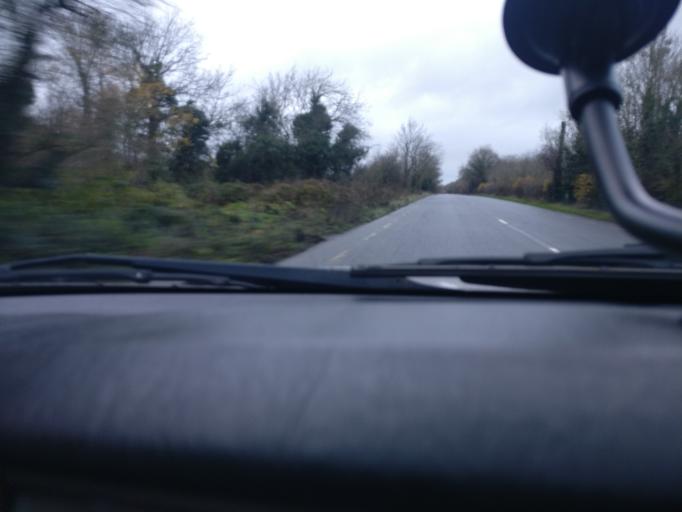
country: IE
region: Leinster
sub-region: Kildare
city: Kilcock
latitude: 53.4143
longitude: -6.7188
